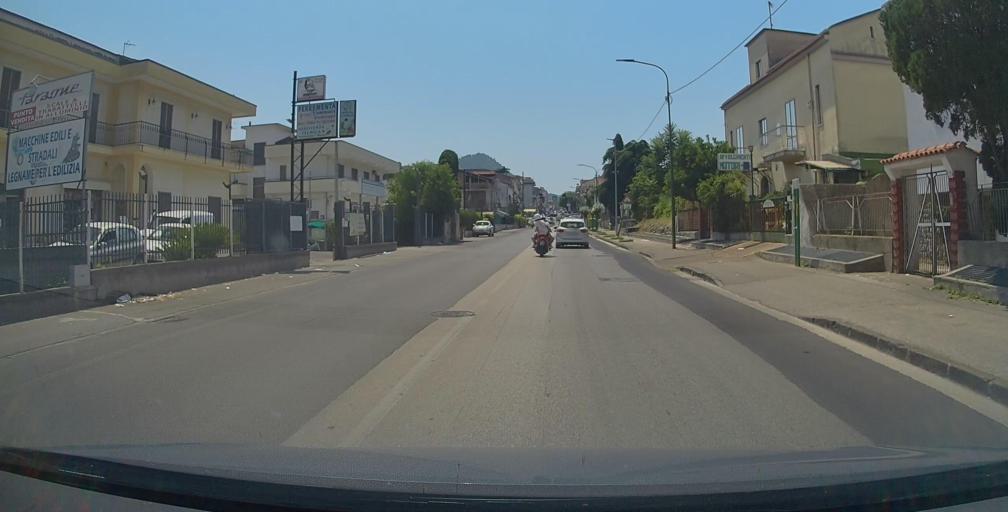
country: IT
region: Campania
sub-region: Provincia di Salerno
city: Cava De Tirreni
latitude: 40.7239
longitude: 14.6943
